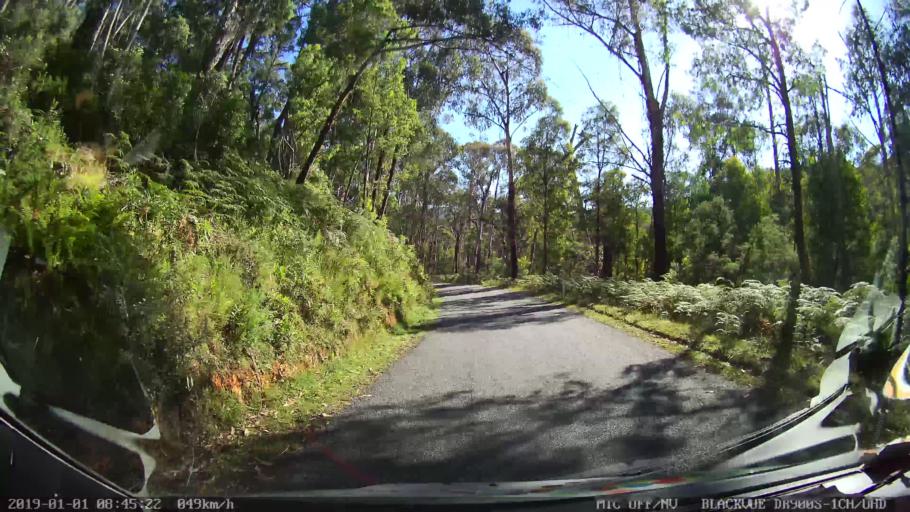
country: AU
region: New South Wales
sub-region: Snowy River
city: Jindabyne
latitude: -36.3059
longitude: 148.1880
